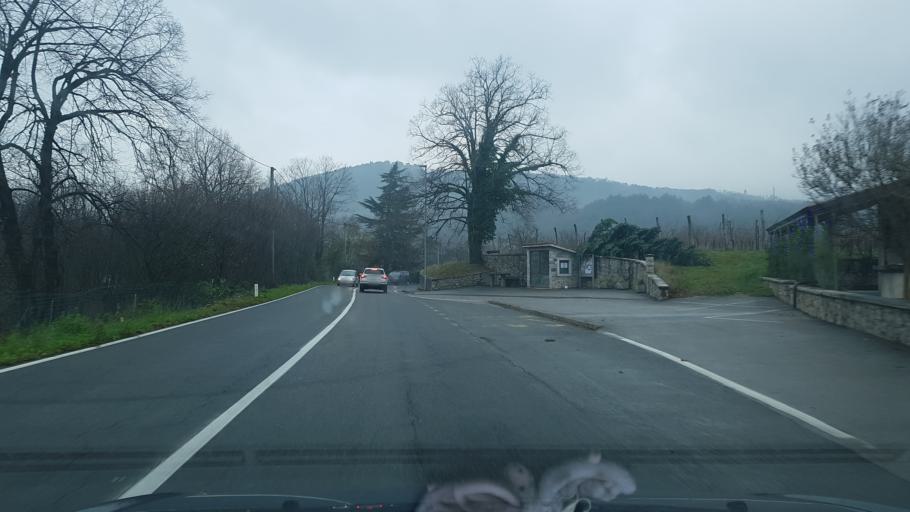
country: SI
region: Sezana
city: Sezana
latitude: 45.7237
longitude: 13.8679
